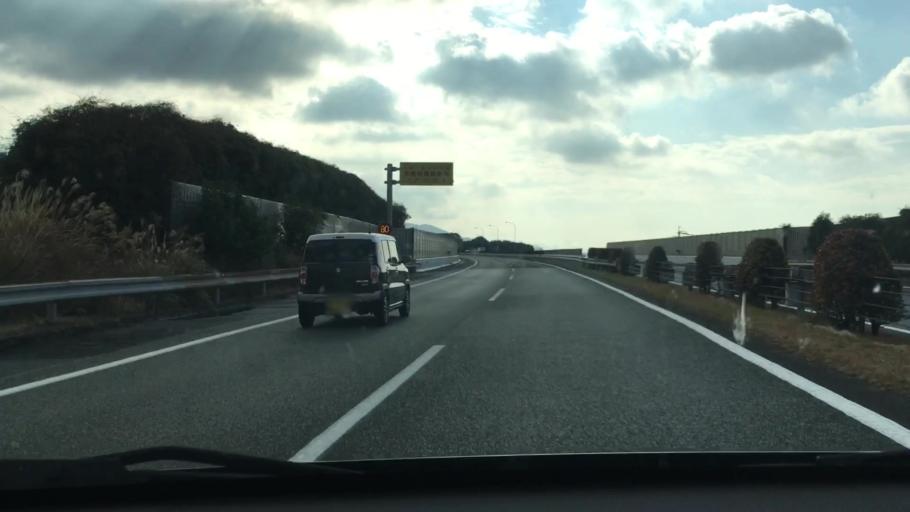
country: JP
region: Kumamoto
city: Yatsushiro
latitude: 32.5178
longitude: 130.6512
